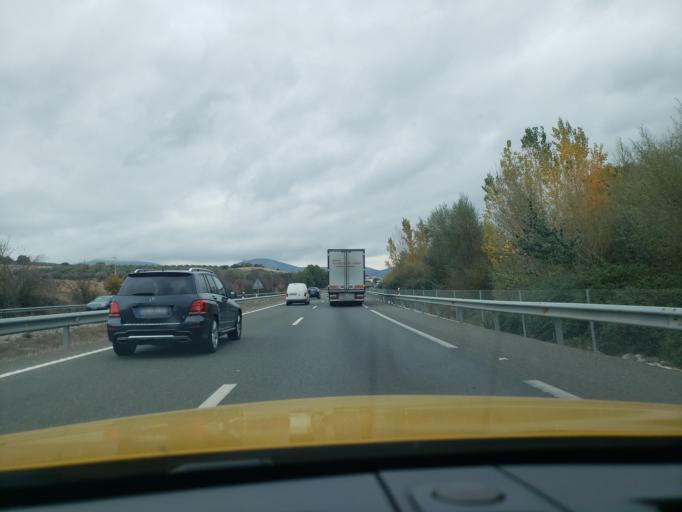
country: ES
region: Andalusia
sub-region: Provincia de Granada
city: Deifontes
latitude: 37.3572
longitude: -3.6122
